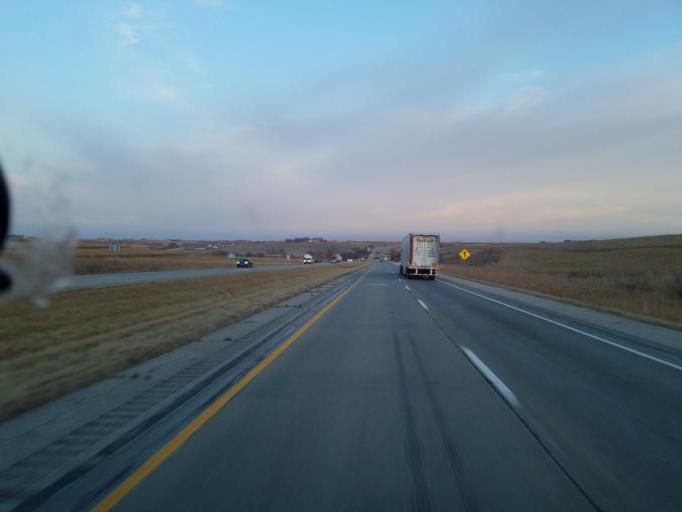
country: US
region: Iowa
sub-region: Pottawattamie County
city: Avoca
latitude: 41.4982
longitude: -95.5439
